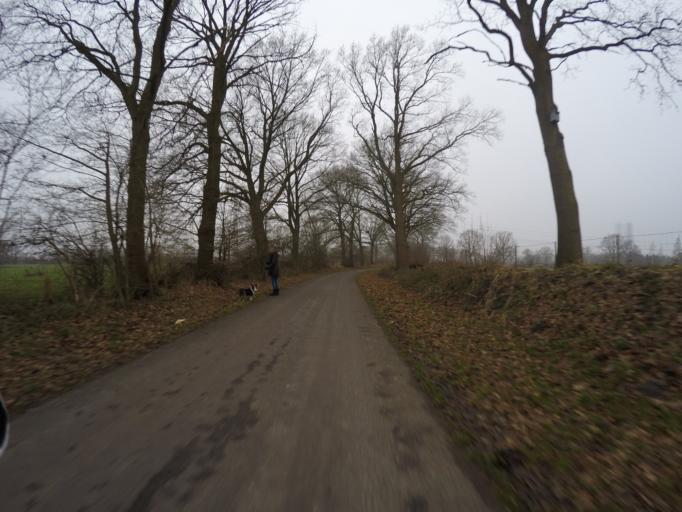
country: DE
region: Schleswig-Holstein
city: Tangstedt
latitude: 53.6725
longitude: 9.8335
